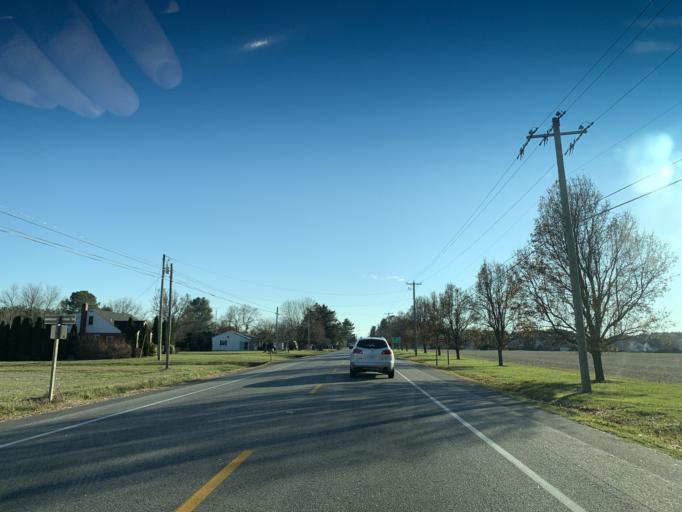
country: US
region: Delaware
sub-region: New Castle County
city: Middletown
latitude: 39.3500
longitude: -75.8780
